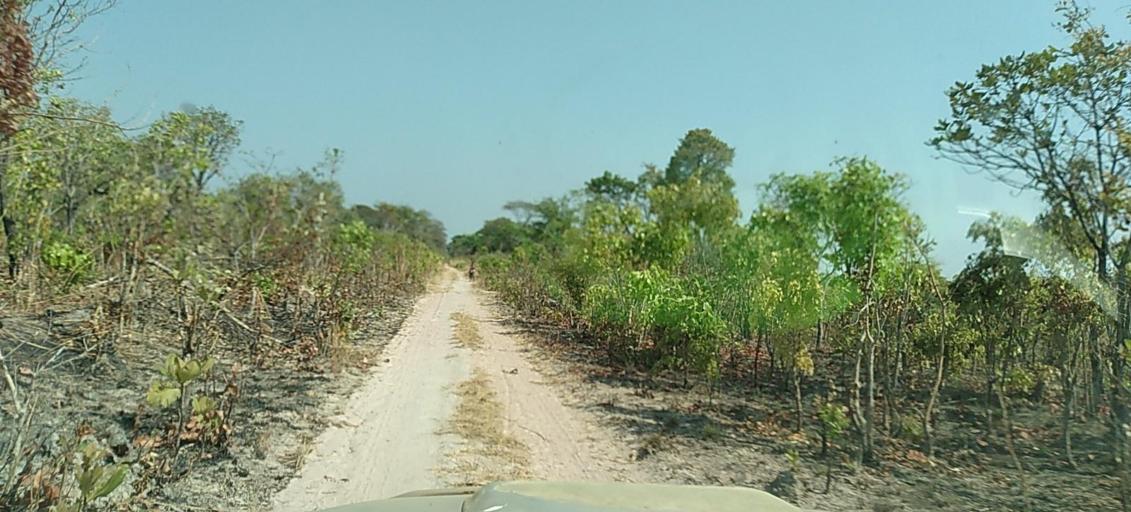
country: ZM
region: North-Western
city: Kalengwa
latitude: -13.3173
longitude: 24.8176
